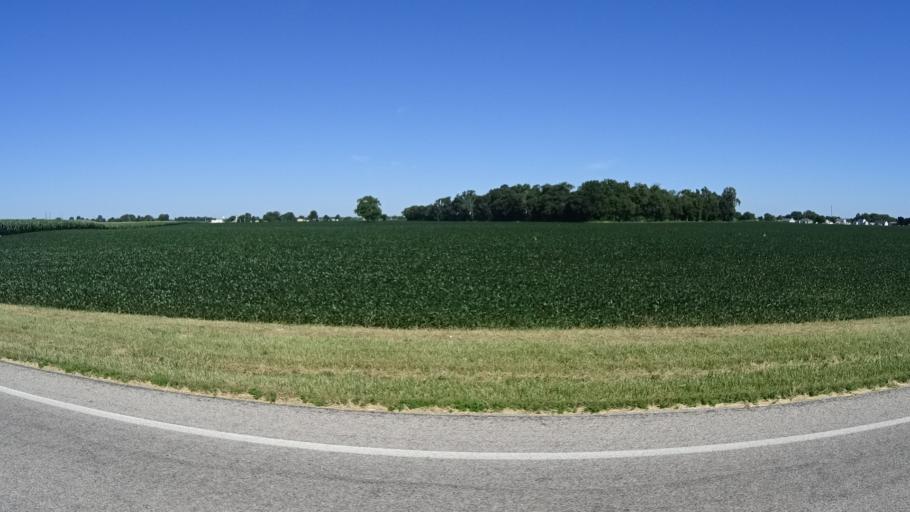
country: US
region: Ohio
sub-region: Erie County
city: Sandusky
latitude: 41.3902
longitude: -82.7211
